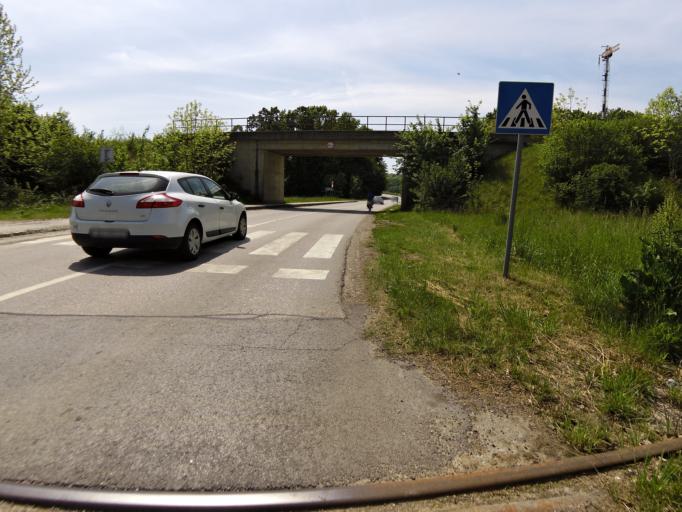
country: HR
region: Karlovacka
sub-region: Grad Karlovac
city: Karlovac
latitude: 45.5483
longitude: 15.5380
